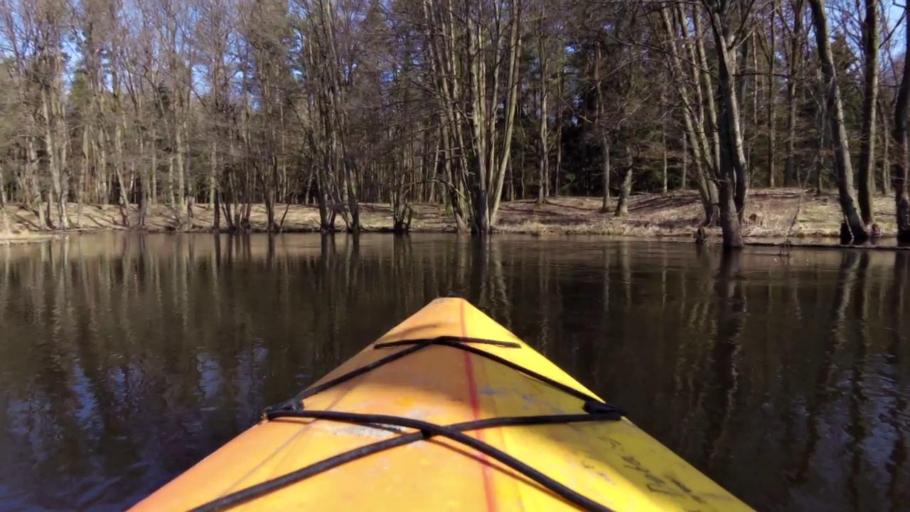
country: PL
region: West Pomeranian Voivodeship
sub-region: Powiat lobeski
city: Radowo Male
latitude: 53.7451
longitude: 15.5177
